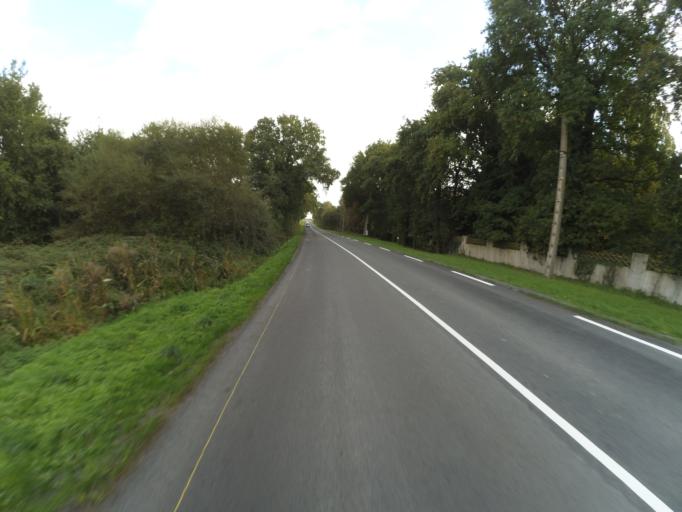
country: FR
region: Pays de la Loire
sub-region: Departement de la Loire-Atlantique
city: Fegreac
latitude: 47.6058
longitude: -2.0314
